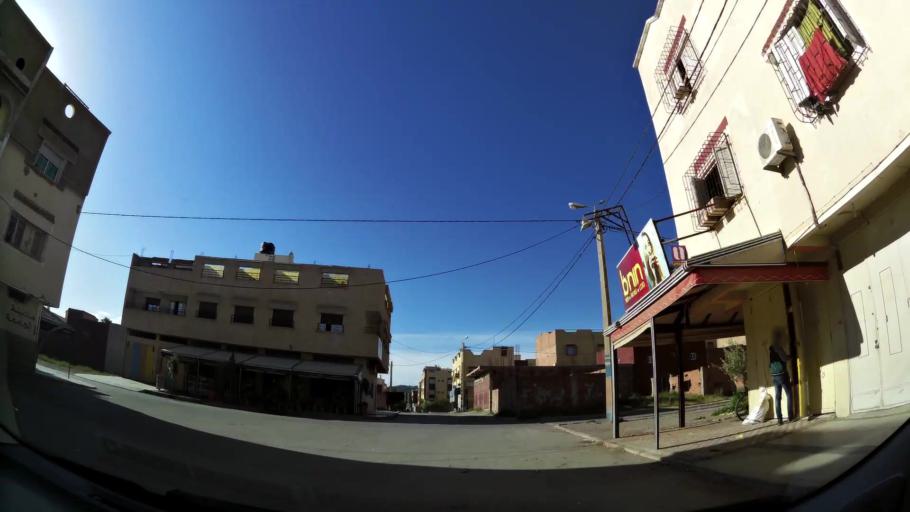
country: MA
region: Oriental
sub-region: Oujda-Angad
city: Oujda
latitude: 34.6588
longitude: -1.9047
